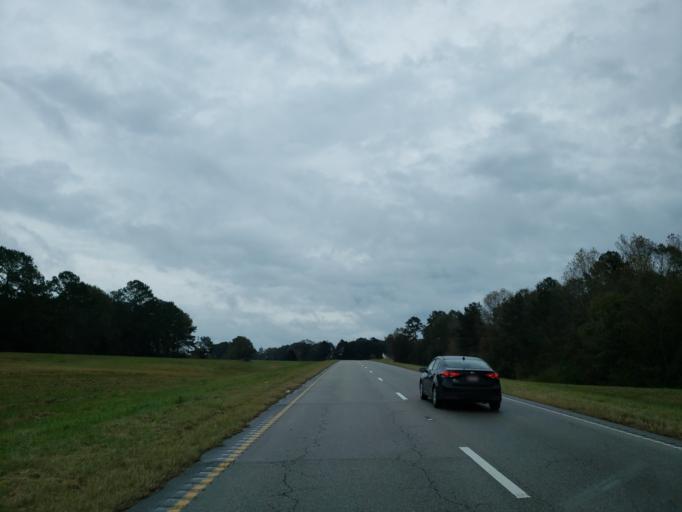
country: US
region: Mississippi
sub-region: Jones County
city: Sharon
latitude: 31.6982
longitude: -88.8967
